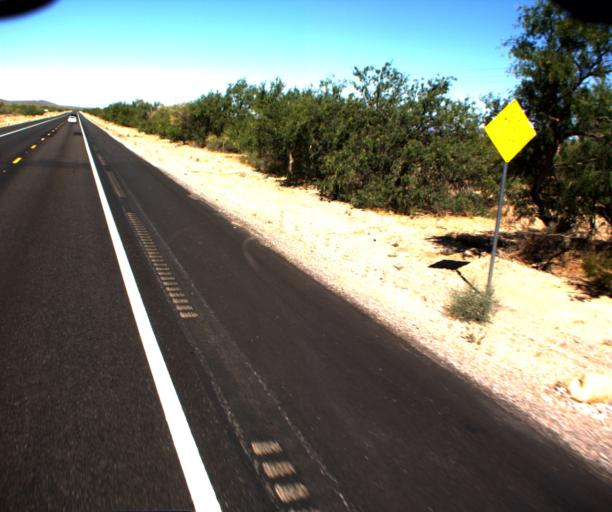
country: US
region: Arizona
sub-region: Pima County
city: Sells
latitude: 31.9237
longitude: -111.8111
